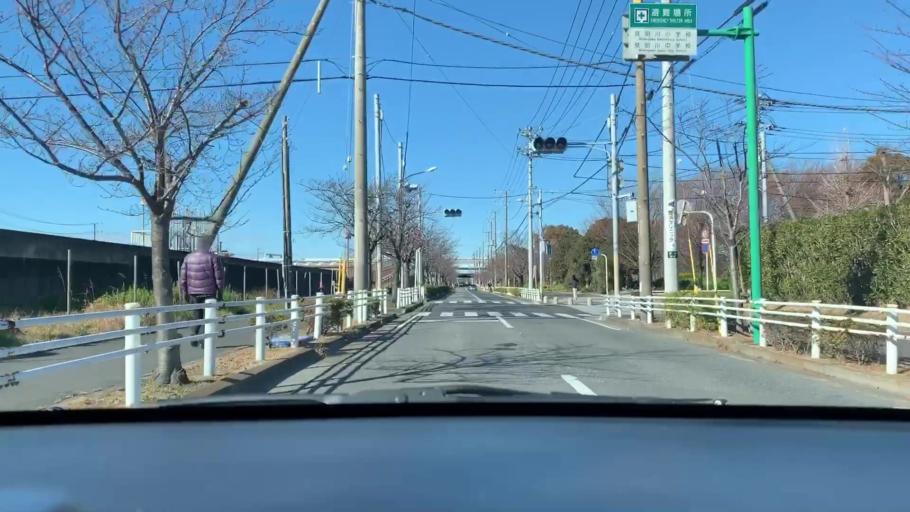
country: JP
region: Tokyo
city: Urayasu
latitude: 35.6366
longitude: 139.8920
